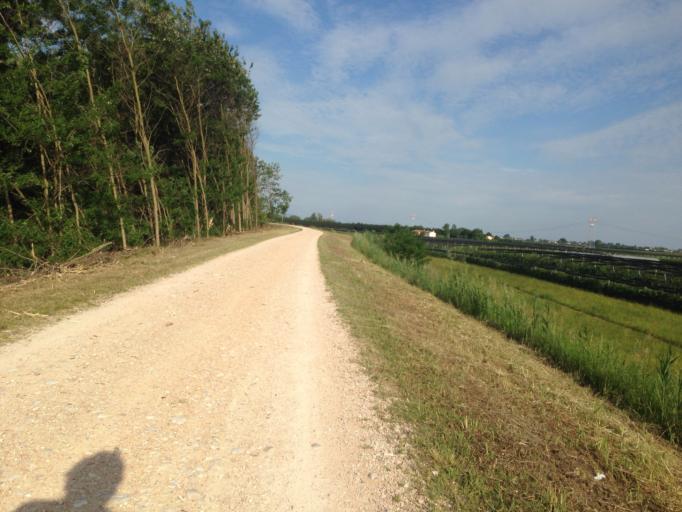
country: IT
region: Veneto
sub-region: Provincia di Verona
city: Zevio
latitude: 45.3717
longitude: 11.1552
